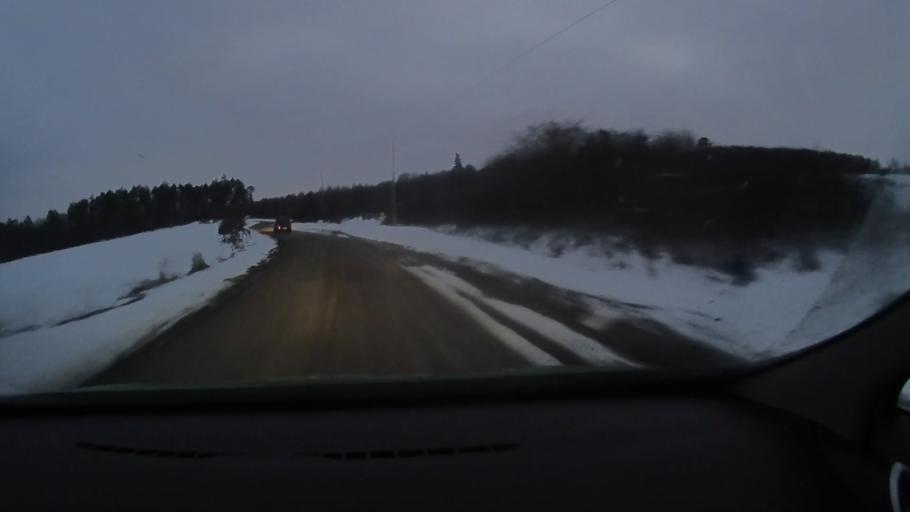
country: RO
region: Harghita
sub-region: Comuna Darjiu
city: Darjiu
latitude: 46.1853
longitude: 25.2477
